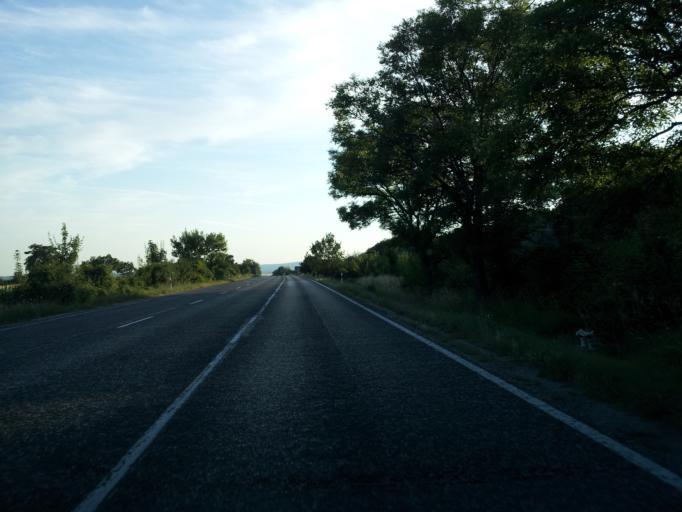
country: HU
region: Fejer
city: Bicske
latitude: 47.4931
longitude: 18.5875
